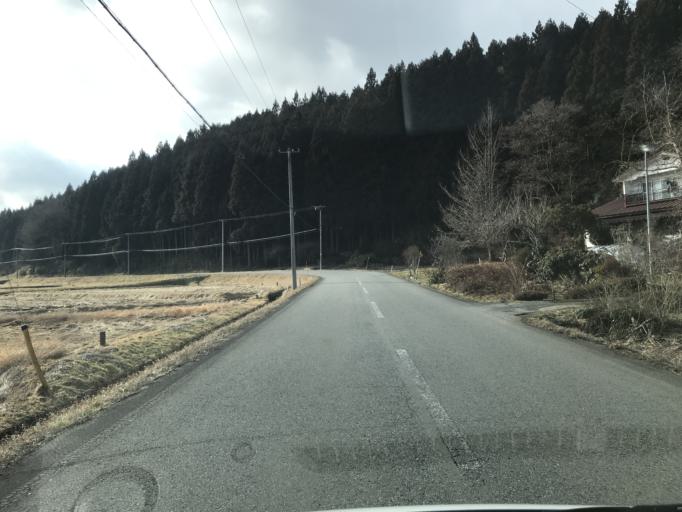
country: JP
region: Iwate
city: Mizusawa
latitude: 39.1489
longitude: 141.0426
